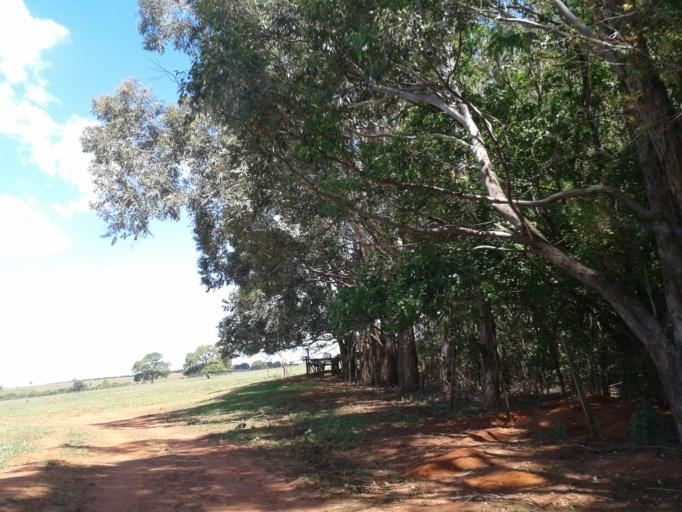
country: BR
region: Minas Gerais
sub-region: Centralina
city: Centralina
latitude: -18.7200
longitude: -49.1574
